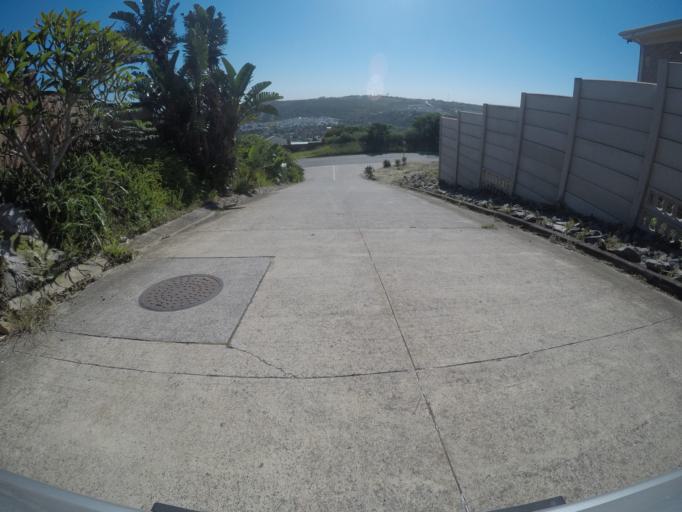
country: ZA
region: Eastern Cape
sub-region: Buffalo City Metropolitan Municipality
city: East London
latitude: -32.9525
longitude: 27.8987
